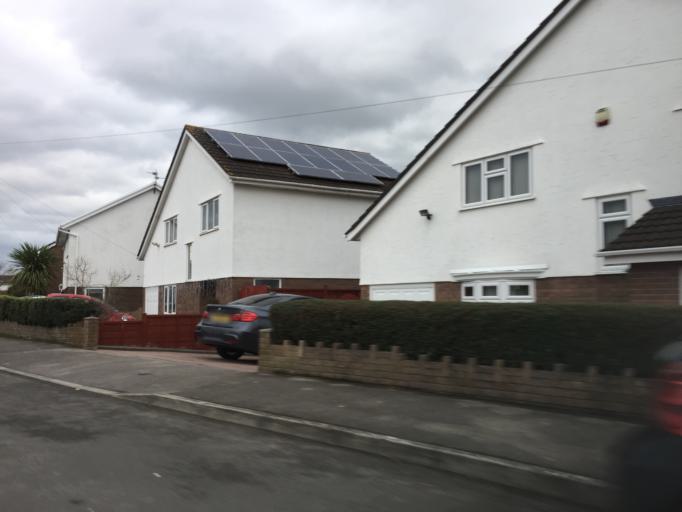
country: GB
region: Wales
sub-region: Monmouthshire
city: Magor
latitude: 51.5808
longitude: -2.8372
